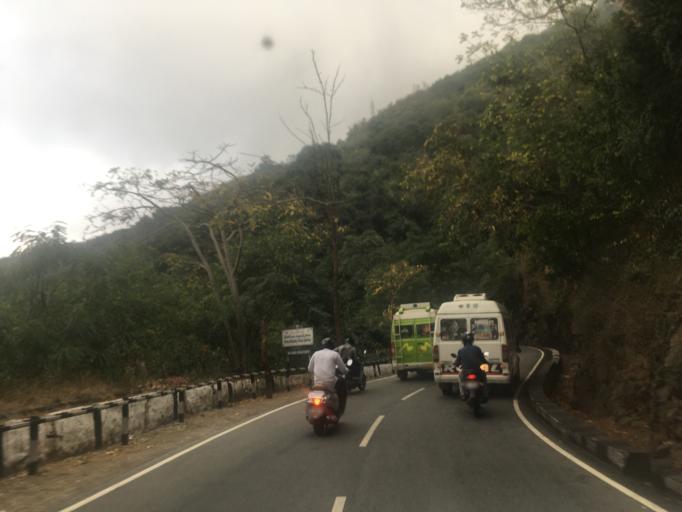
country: IN
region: Andhra Pradesh
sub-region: Chittoor
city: Tirumala
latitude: 13.6648
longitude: 79.3485
